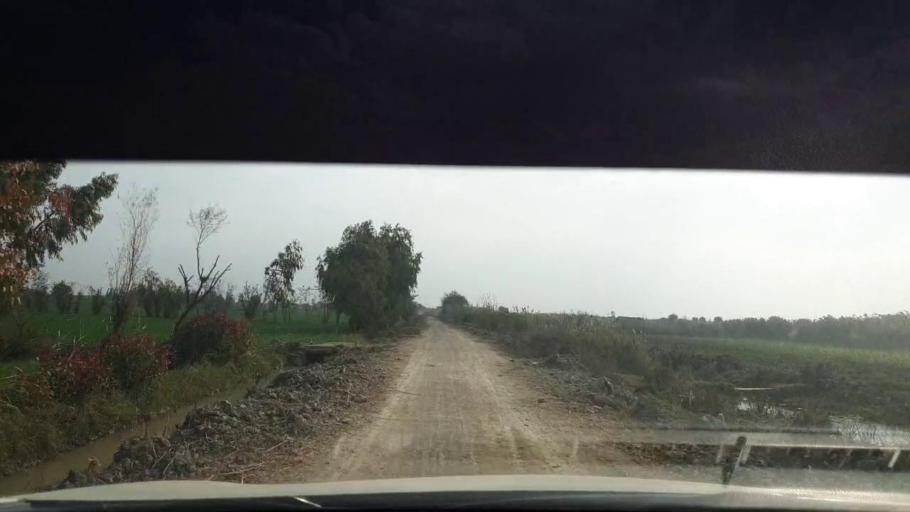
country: PK
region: Sindh
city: Berani
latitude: 25.7512
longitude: 68.8770
